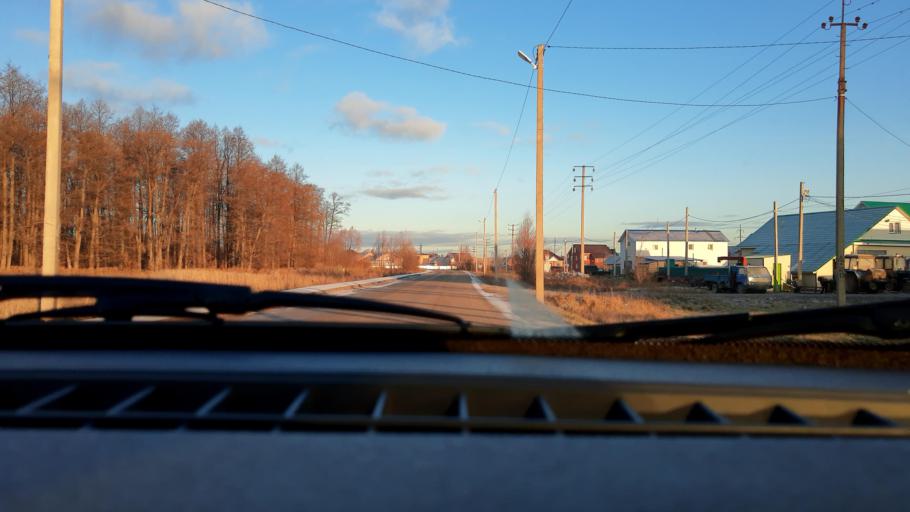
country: RU
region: Bashkortostan
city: Mikhaylovka
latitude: 54.7819
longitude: 55.8215
